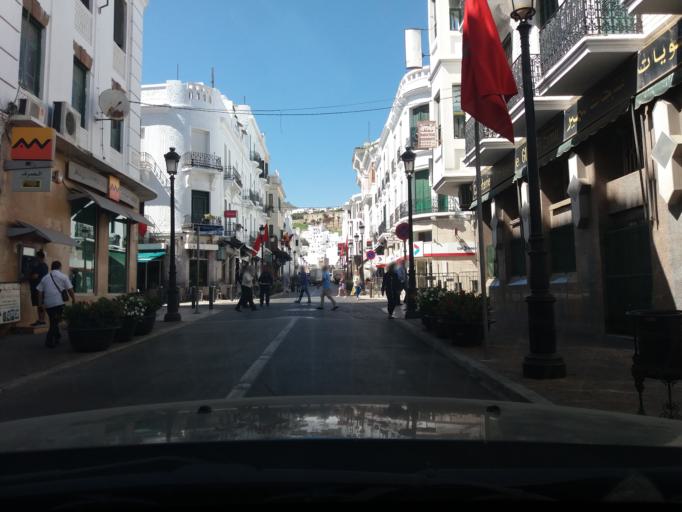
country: MA
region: Tanger-Tetouan
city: Tetouan
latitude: 35.5699
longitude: -5.3721
